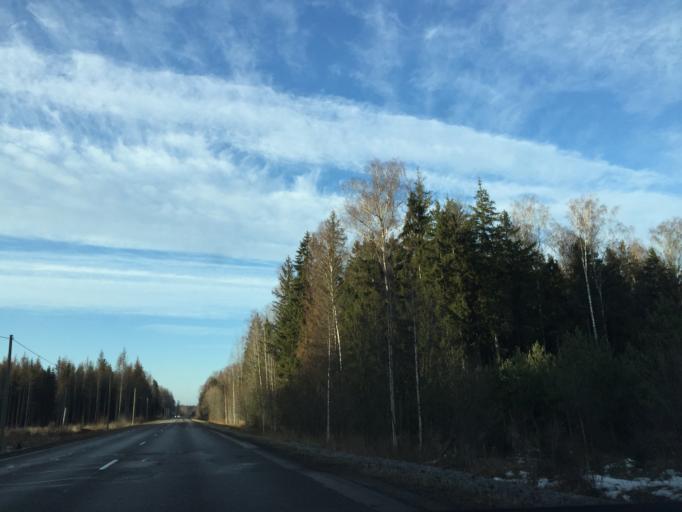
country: LV
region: Kekava
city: Balozi
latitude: 56.8048
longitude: 24.0711
